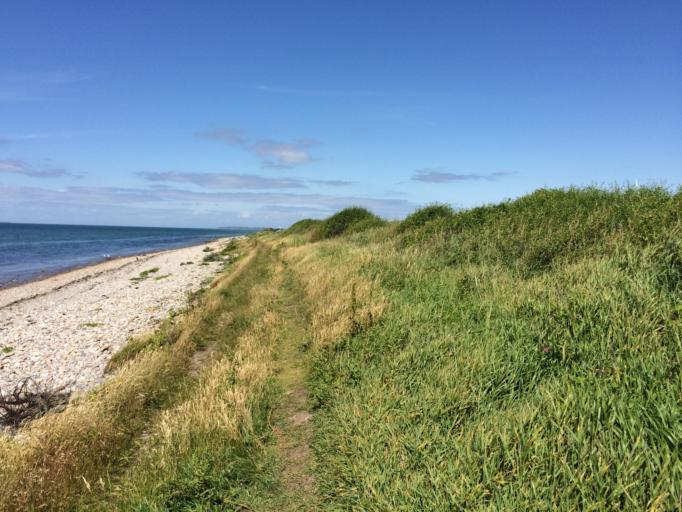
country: DK
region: Central Jutland
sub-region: Samso Kommune
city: Tranebjerg
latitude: 55.8344
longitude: 10.5276
